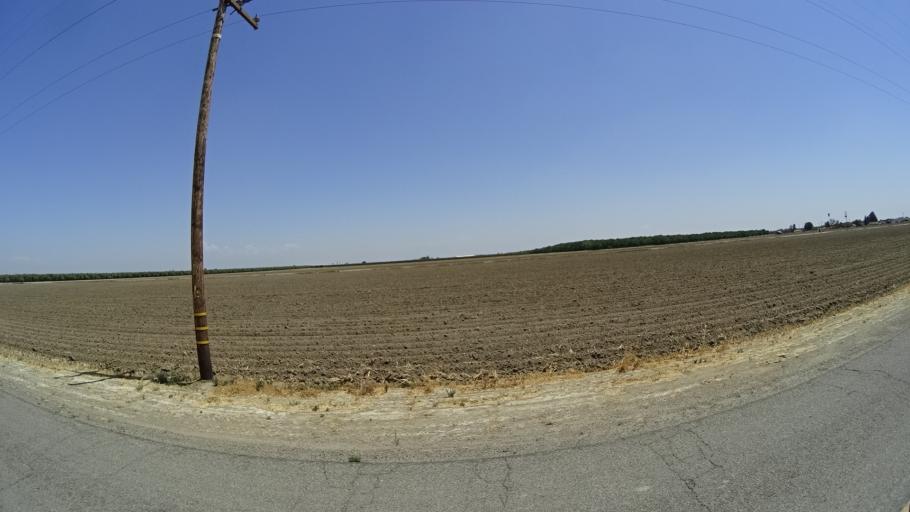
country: US
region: California
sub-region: Kings County
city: Armona
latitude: 36.3624
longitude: -119.7270
